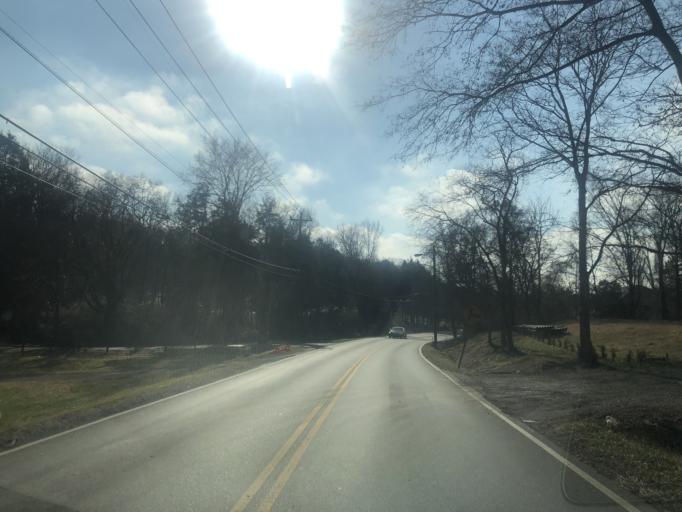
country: US
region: Tennessee
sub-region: Rutherford County
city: La Vergne
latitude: 36.0632
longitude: -86.6637
